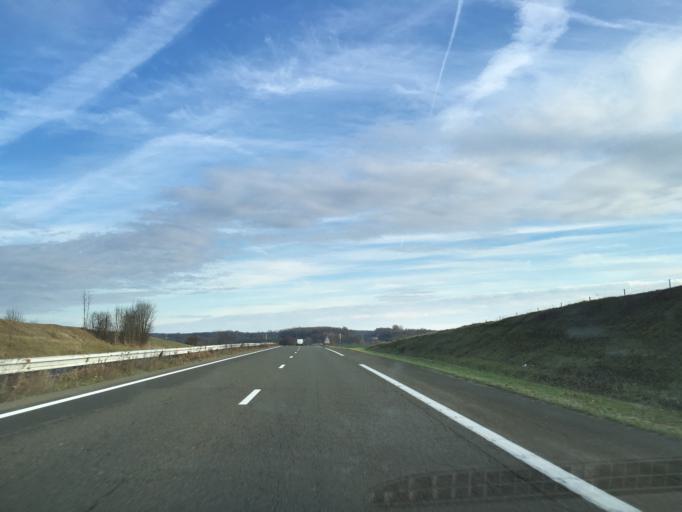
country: FR
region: Picardie
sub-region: Departement de l'Aisne
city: Essomes-sur-Marne
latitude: 49.0509
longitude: 3.3099
